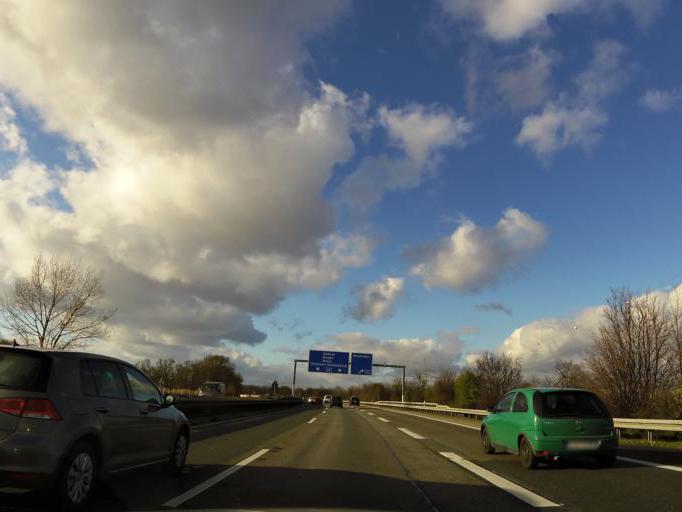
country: DE
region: Hesse
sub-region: Regierungsbezirk Darmstadt
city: Ginsheim-Gustavsburg
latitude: 49.9806
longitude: 8.3473
